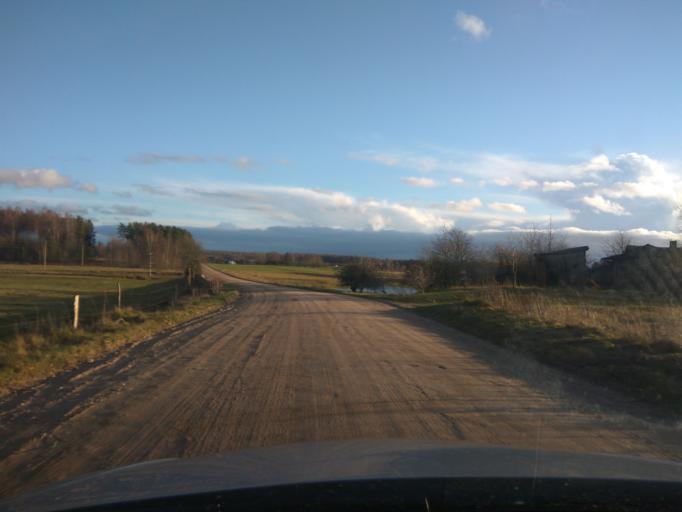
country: LV
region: Aizpute
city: Aizpute
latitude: 56.7652
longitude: 21.7110
